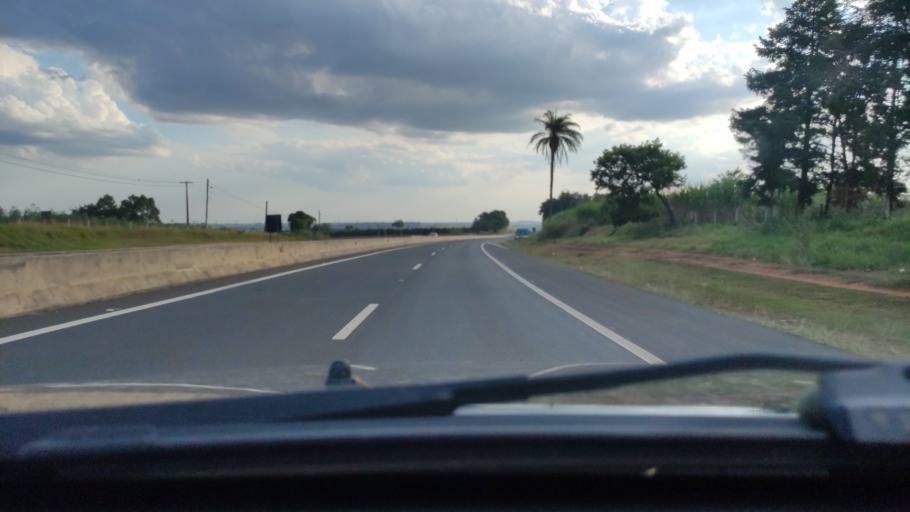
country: BR
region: Sao Paulo
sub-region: Artur Nogueira
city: Artur Nogueira
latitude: -22.4669
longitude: -47.1094
